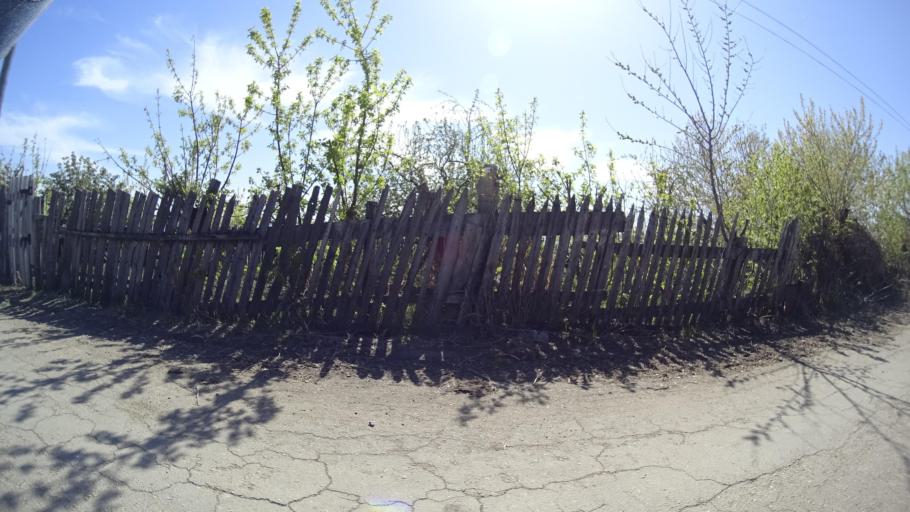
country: RU
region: Chelyabinsk
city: Chesma
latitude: 53.7962
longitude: 61.0267
